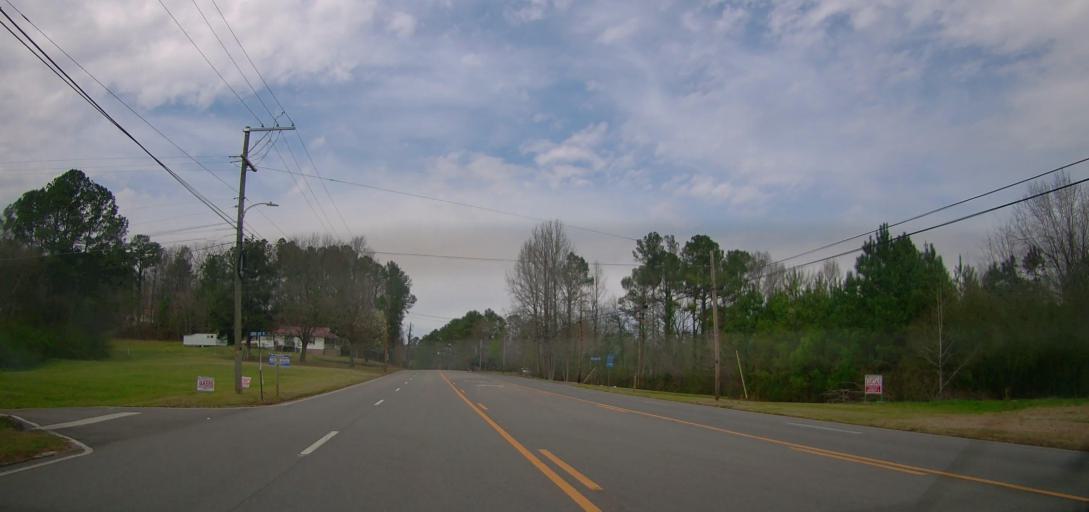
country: US
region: Alabama
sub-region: Marion County
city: Guin
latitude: 33.9797
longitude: -87.9176
